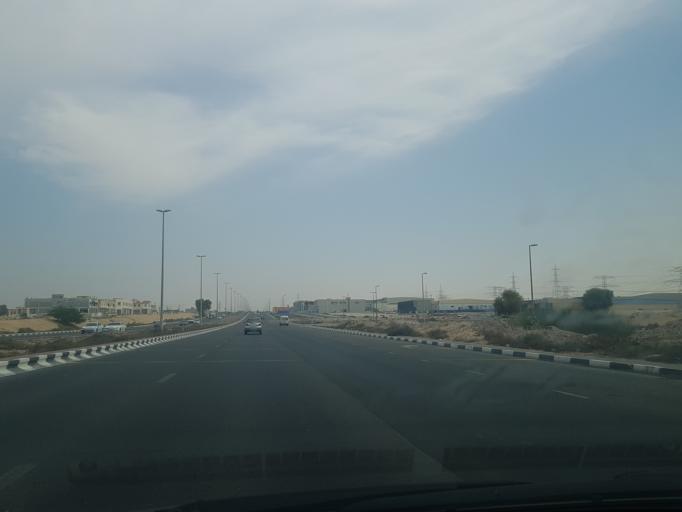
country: AE
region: Ash Shariqah
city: Sharjah
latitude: 25.2476
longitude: 55.5417
